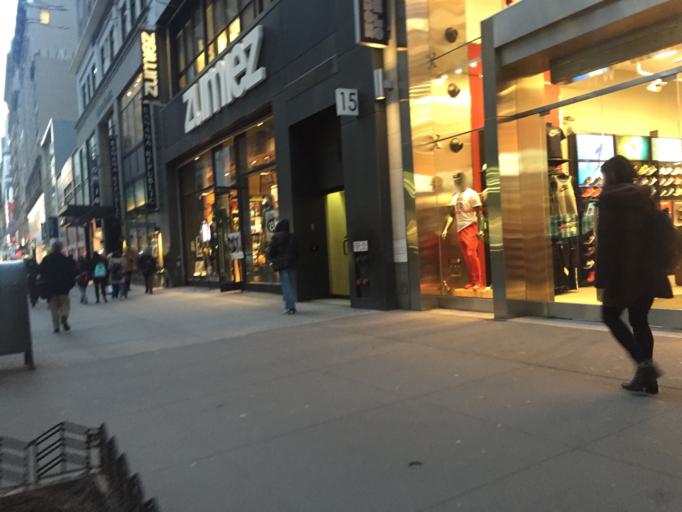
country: US
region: New York
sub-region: Queens County
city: Long Island City
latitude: 40.7489
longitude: -73.9856
